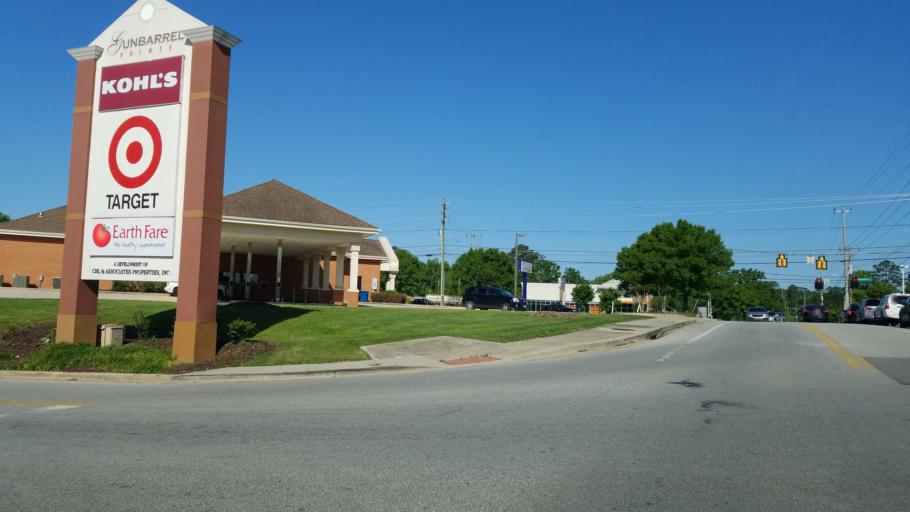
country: US
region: Tennessee
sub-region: Hamilton County
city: East Brainerd
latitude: 35.0265
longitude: -85.1564
